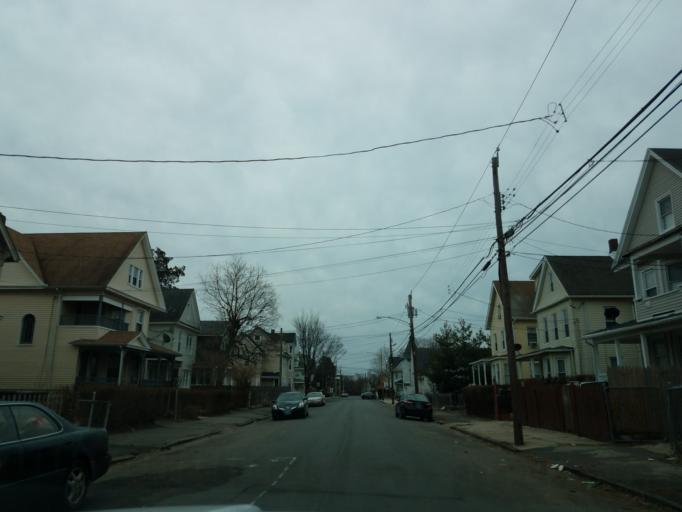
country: US
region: Connecticut
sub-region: Fairfield County
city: Stratford
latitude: 41.1808
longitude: -73.1673
